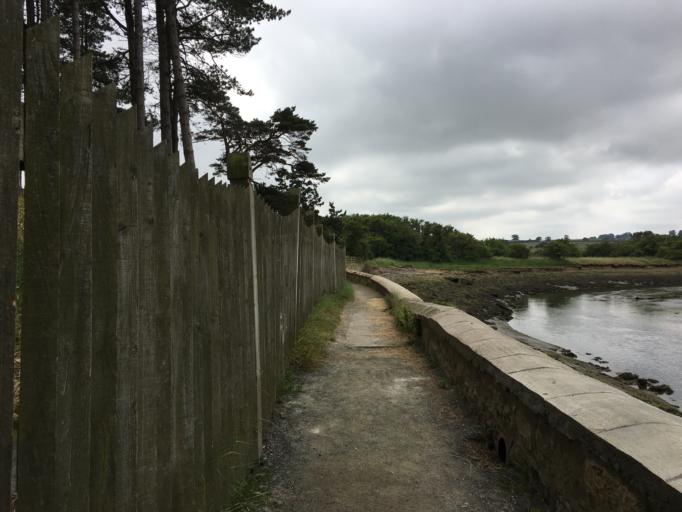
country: GB
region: England
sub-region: Northumberland
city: Alnmouth
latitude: 55.3896
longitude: -1.6174
